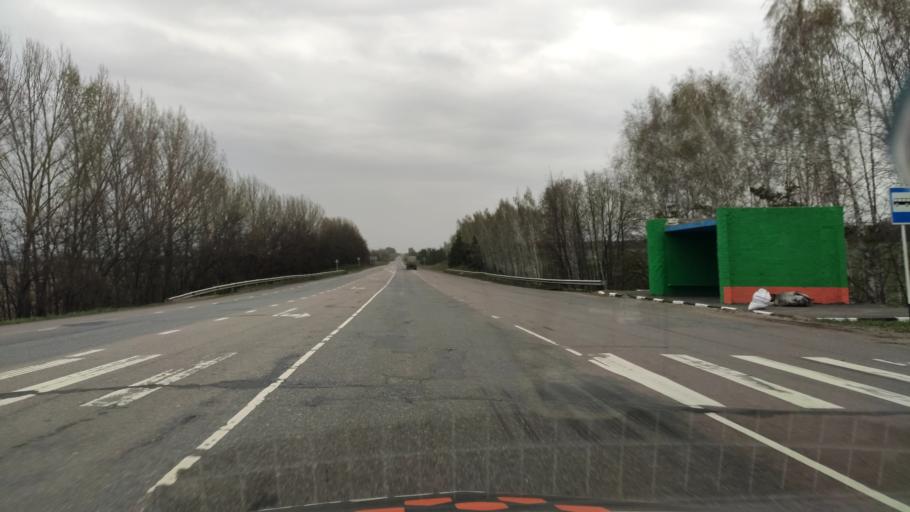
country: RU
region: Belgorod
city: Staryy Oskol
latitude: 51.4363
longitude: 37.9041
